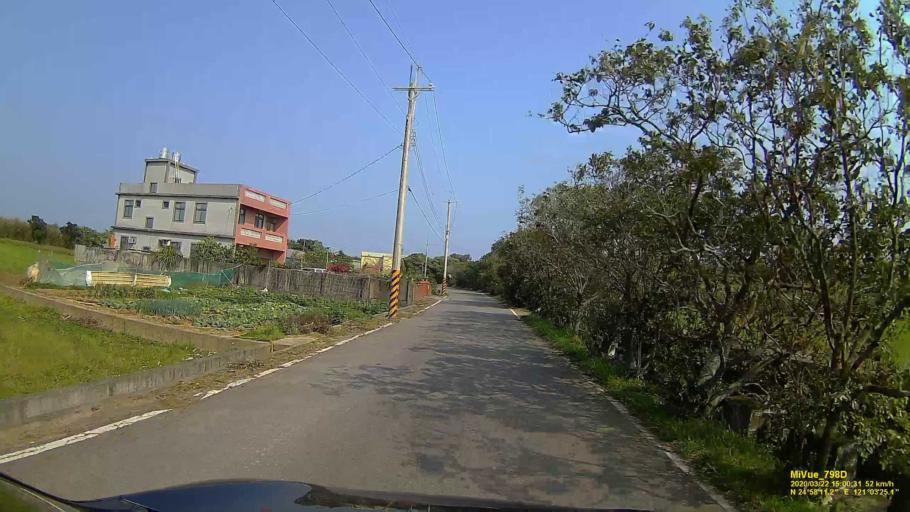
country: TW
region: Taiwan
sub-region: Hsinchu
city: Zhubei
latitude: 24.9696
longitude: 121.0574
